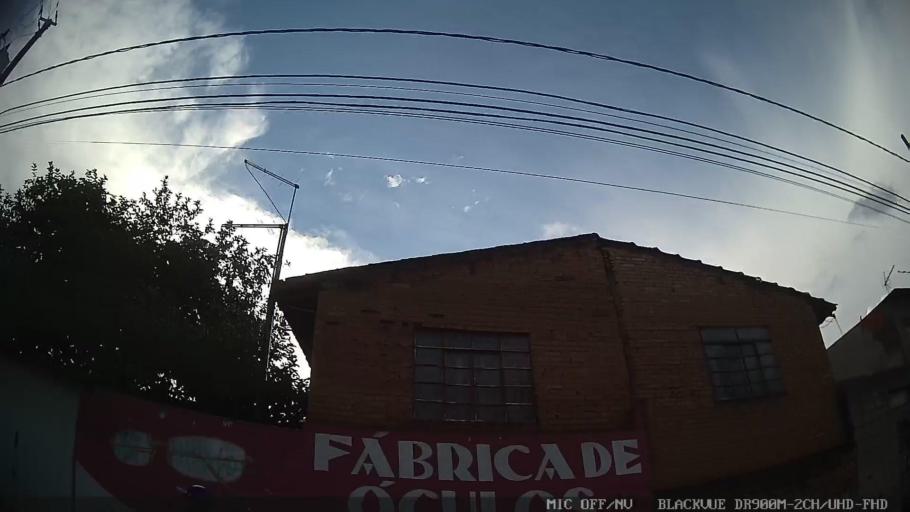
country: BR
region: Sao Paulo
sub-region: Braganca Paulista
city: Braganca Paulista
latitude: -22.9157
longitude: -46.5503
